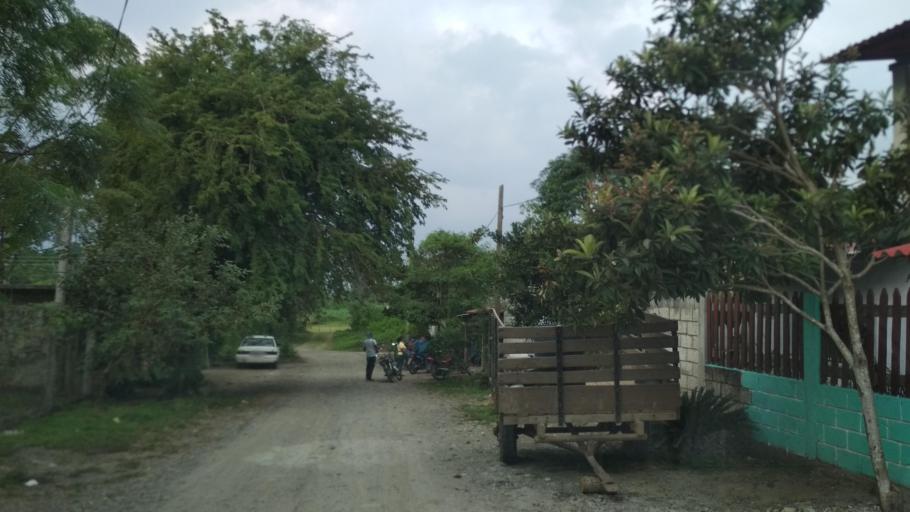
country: MM
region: Kayah
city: Loikaw
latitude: 20.2410
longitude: 97.2763
